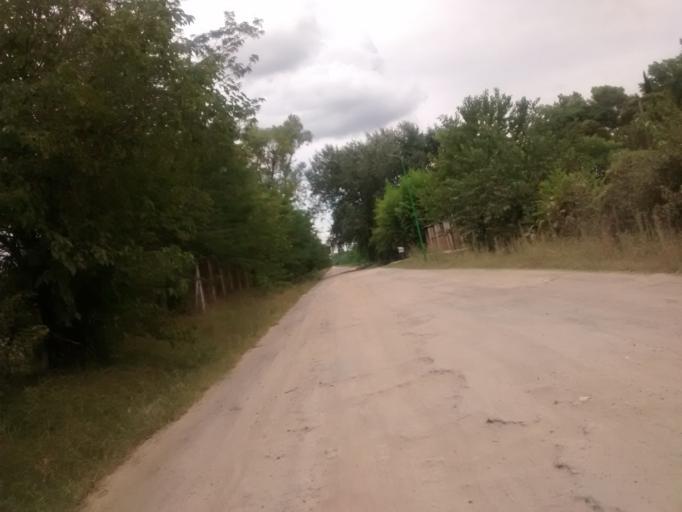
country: AR
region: Buenos Aires
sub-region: Partido de La Plata
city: La Plata
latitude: -34.8602
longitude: -58.0735
